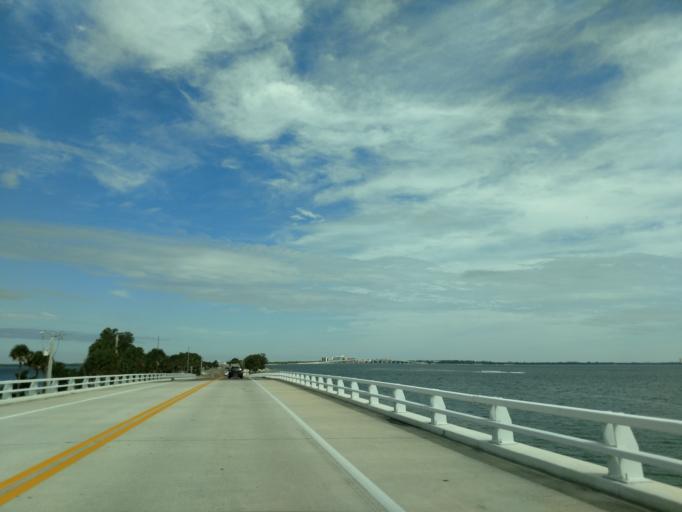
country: US
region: Florida
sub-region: Lee County
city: Sanibel
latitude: 26.4629
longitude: -82.0319
